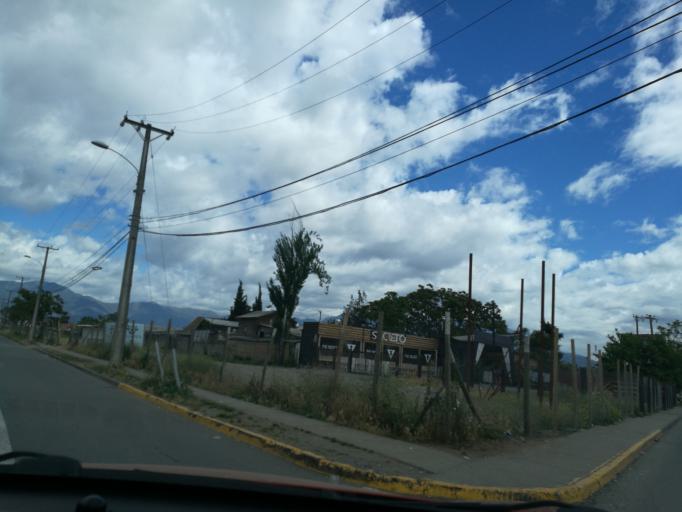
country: CL
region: O'Higgins
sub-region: Provincia de Cachapoal
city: Rancagua
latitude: -34.1450
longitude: -70.7293
